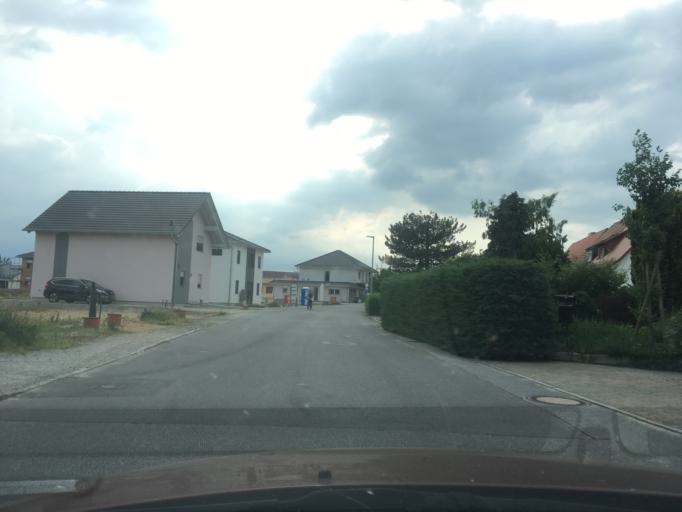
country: DE
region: Saxony
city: Bautzen
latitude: 51.1703
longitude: 14.4494
